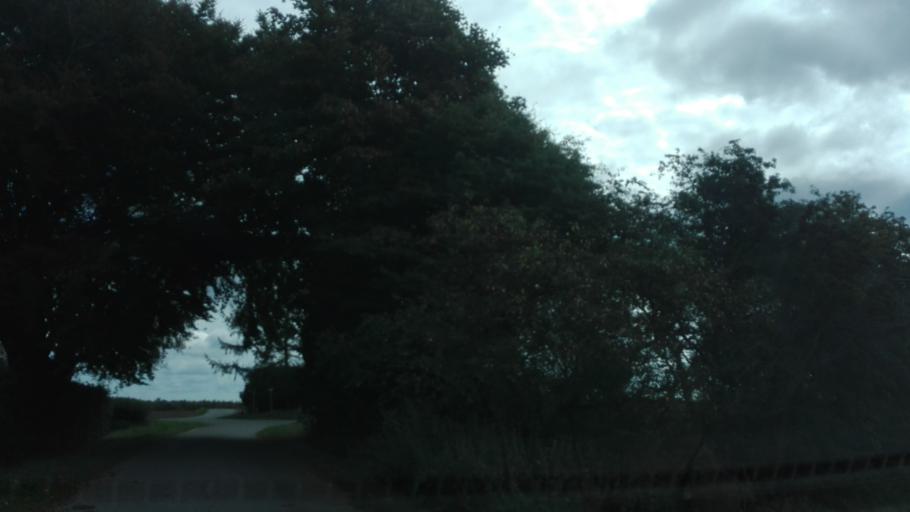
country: DK
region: Central Jutland
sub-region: Skanderborg Kommune
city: Horning
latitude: 56.0922
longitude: 10.0112
